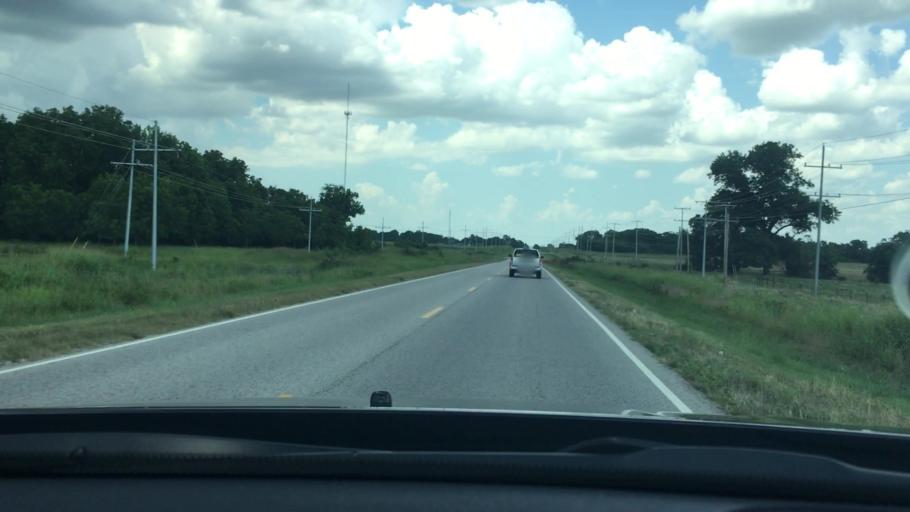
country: US
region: Oklahoma
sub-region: Pontotoc County
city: Ada
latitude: 34.6467
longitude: -96.6349
